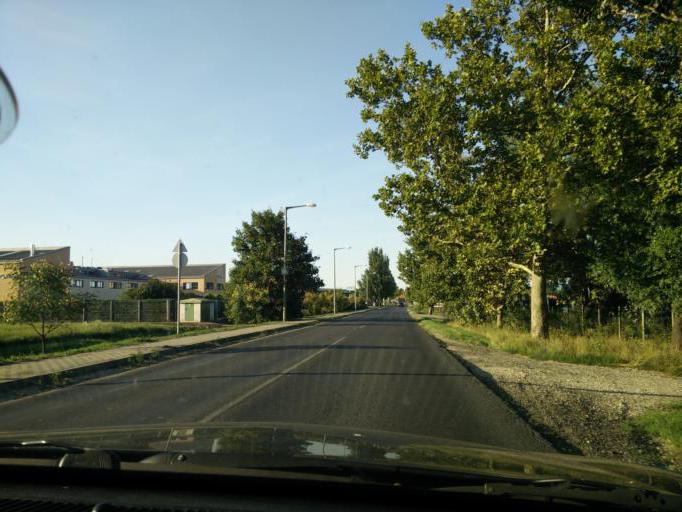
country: HU
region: Pest
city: Zsambek
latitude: 47.5390
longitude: 18.7232
